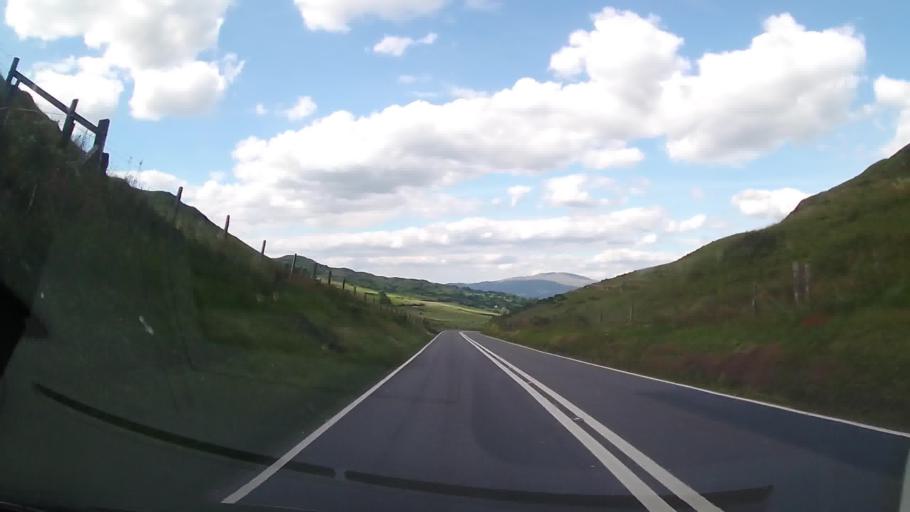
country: GB
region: Wales
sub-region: Gwynedd
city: Dolgellau
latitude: 52.7092
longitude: -3.8416
